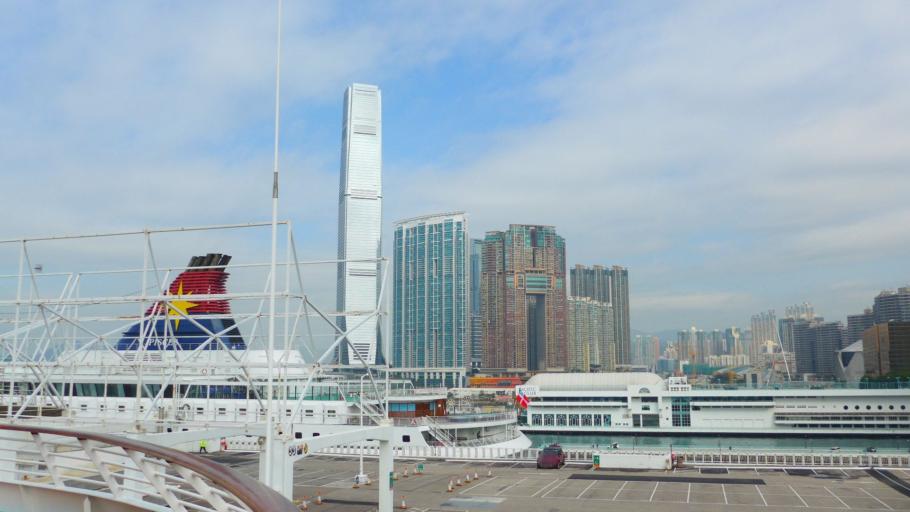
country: HK
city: Hong Kong
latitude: 22.2943
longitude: 114.1674
